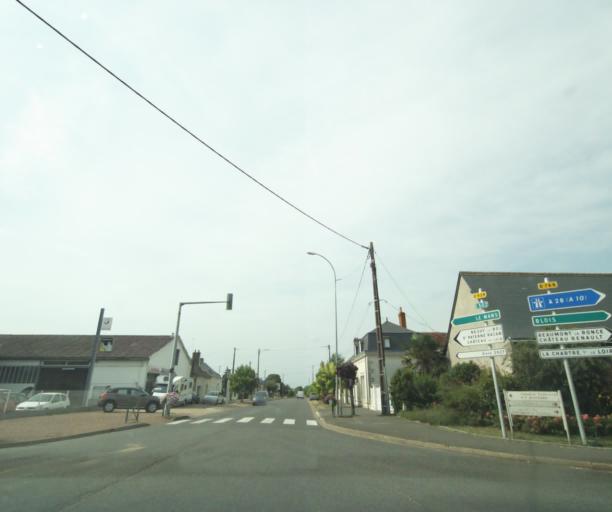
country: FR
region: Centre
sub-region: Departement d'Indre-et-Loire
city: Neuille-Pont-Pierre
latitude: 47.5477
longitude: 0.5513
